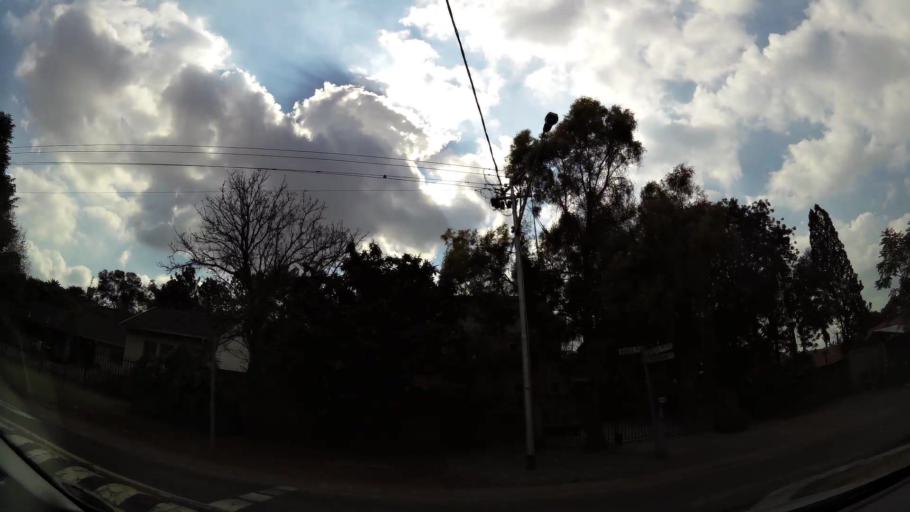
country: ZA
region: Gauteng
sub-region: City of Tshwane Metropolitan Municipality
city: Pretoria
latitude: -25.7495
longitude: 28.3150
